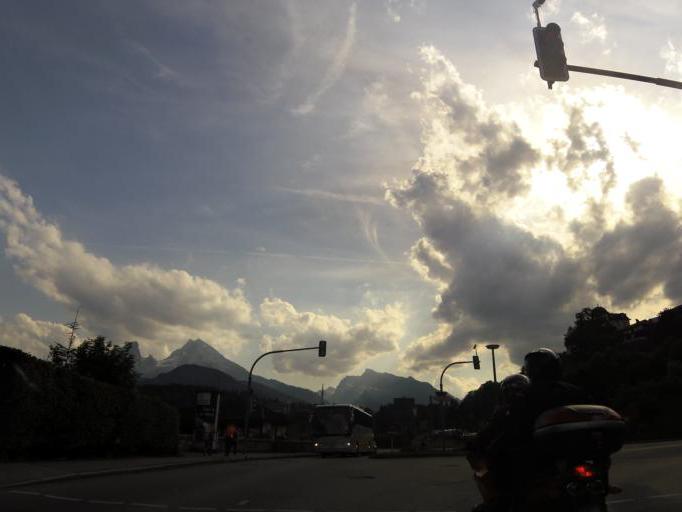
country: DE
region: Bavaria
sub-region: Upper Bavaria
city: Berchtesgaden
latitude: 47.6286
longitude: 13.0032
